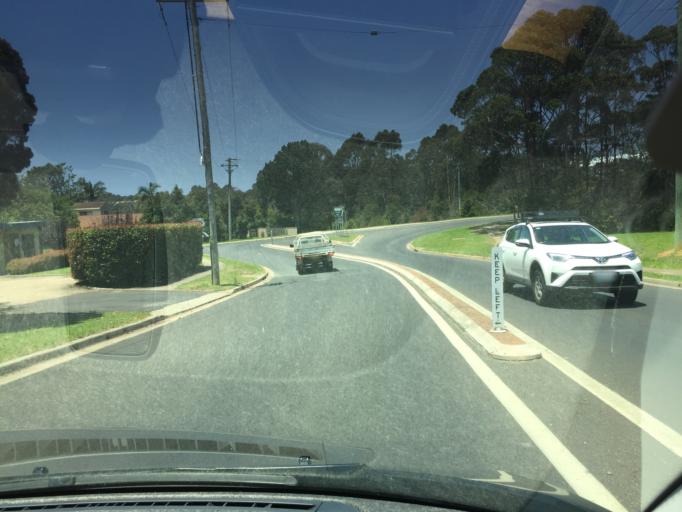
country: AU
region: New South Wales
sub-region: Bega Valley
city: Merimbula
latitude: -36.8832
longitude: 149.9066
